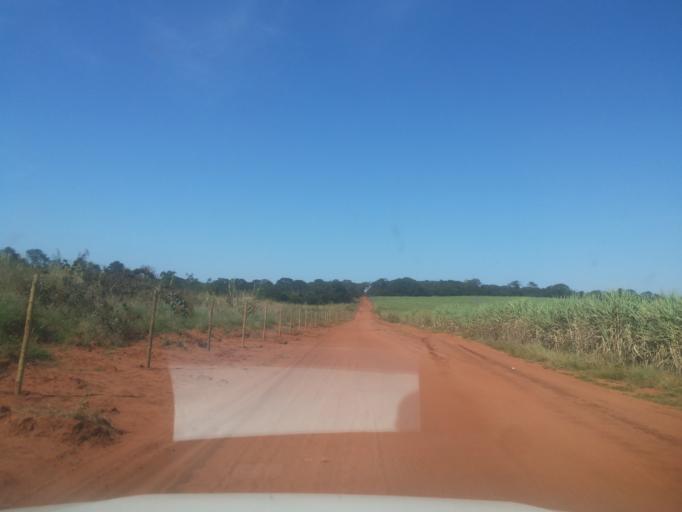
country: BR
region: Minas Gerais
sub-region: Santa Vitoria
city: Santa Vitoria
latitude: -19.0004
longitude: -50.3737
